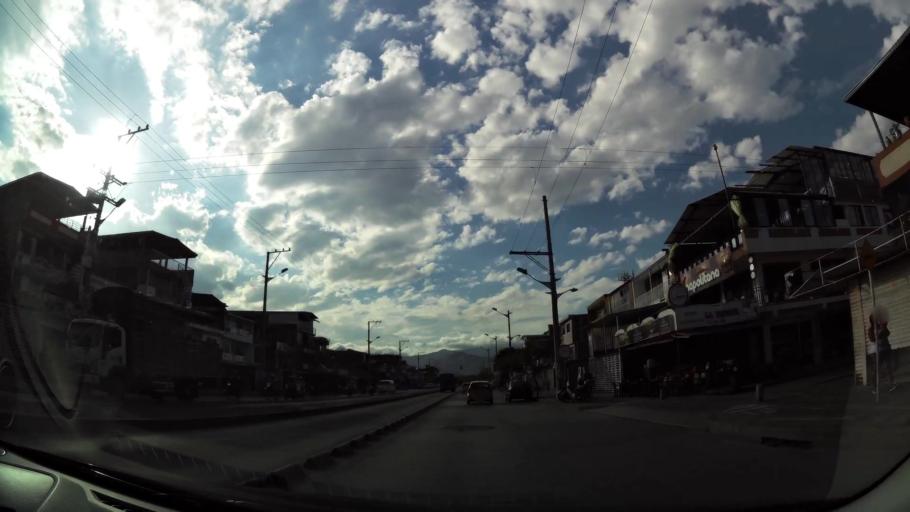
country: CO
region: Valle del Cauca
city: Cali
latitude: 3.4229
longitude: -76.4923
